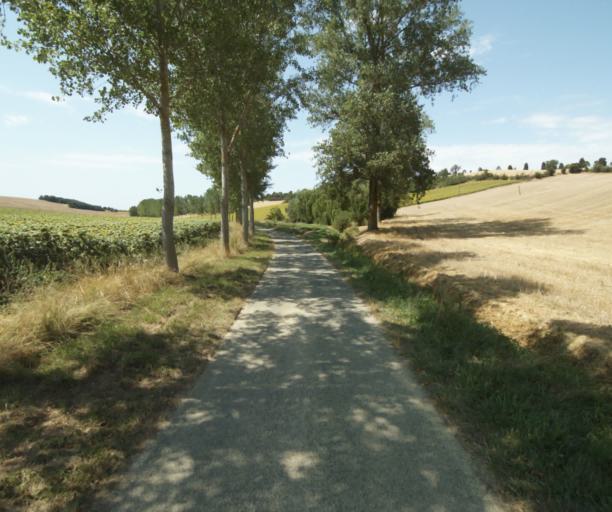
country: FR
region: Midi-Pyrenees
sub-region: Departement de la Haute-Garonne
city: Saint-Felix-Lauragais
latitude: 43.4571
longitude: 1.8788
